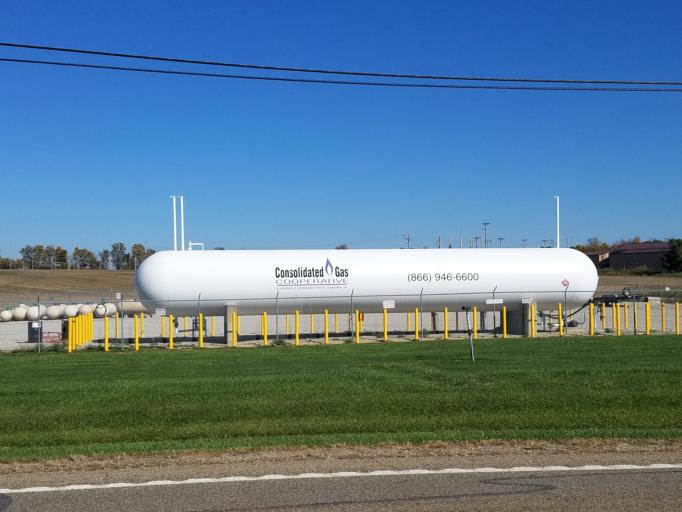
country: US
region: Ohio
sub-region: Morrow County
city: Mount Gilead
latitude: 40.5330
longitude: -82.7668
